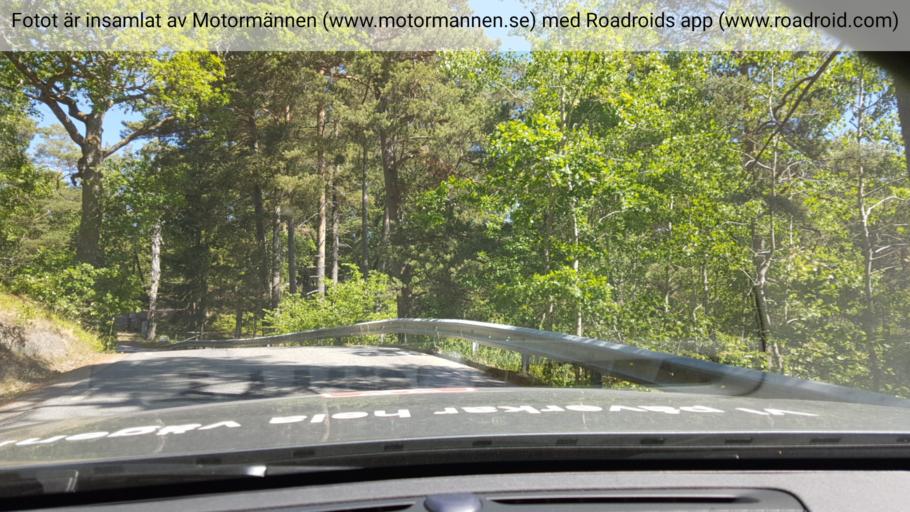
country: SE
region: Stockholm
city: Dalaro
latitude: 59.1609
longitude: 18.4488
